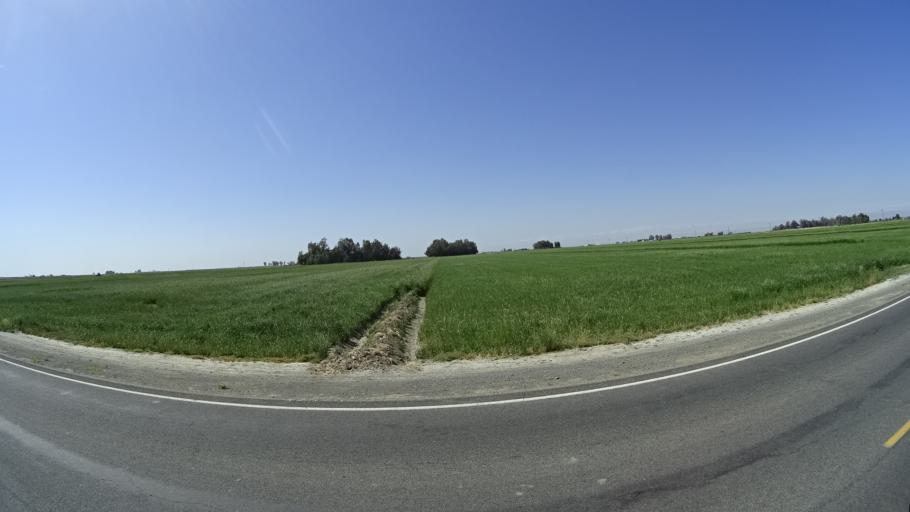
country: US
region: California
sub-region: Kings County
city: Stratford
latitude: 36.2113
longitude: -119.7759
